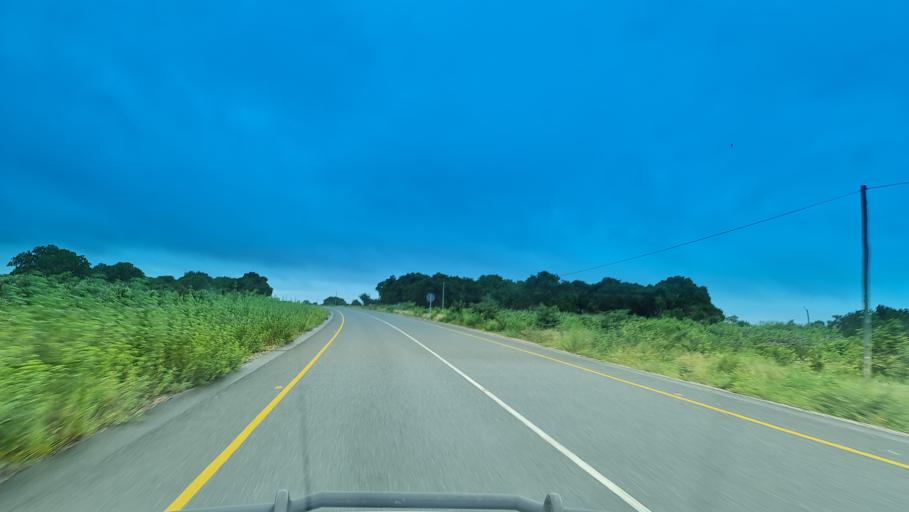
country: MZ
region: Nampula
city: Nampula
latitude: -15.6053
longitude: 39.3279
